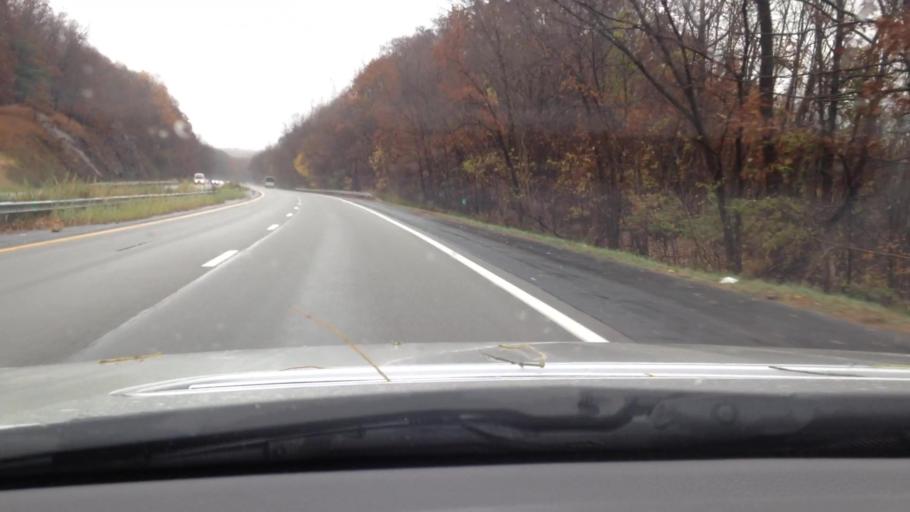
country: US
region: New York
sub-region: Westchester County
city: Crugers
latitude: 41.2439
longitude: -73.9192
